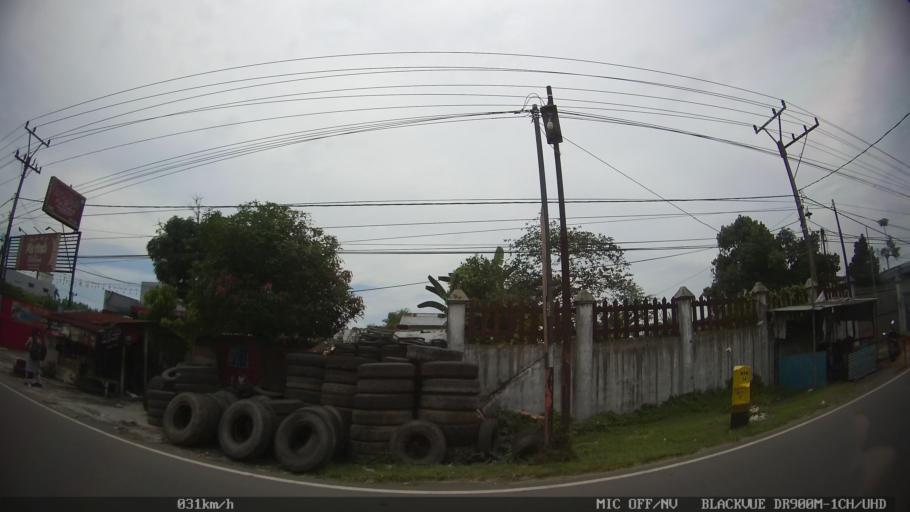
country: ID
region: North Sumatra
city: Sunggal
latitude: 3.5995
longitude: 98.5584
